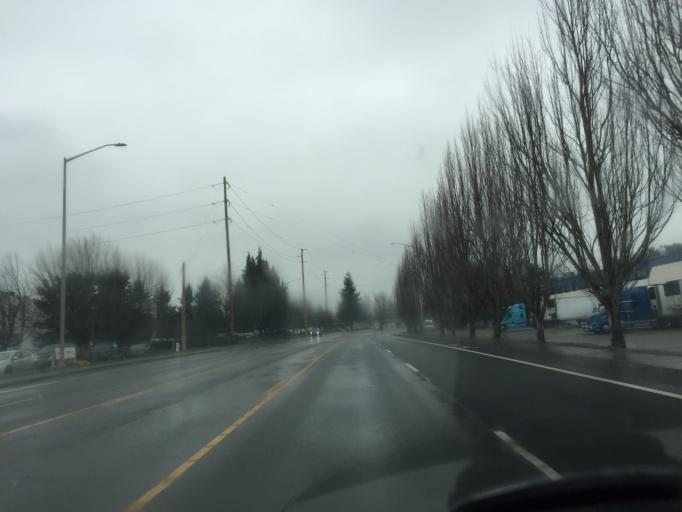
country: US
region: Washington
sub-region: King County
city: SeaTac
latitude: 47.4247
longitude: -122.2632
